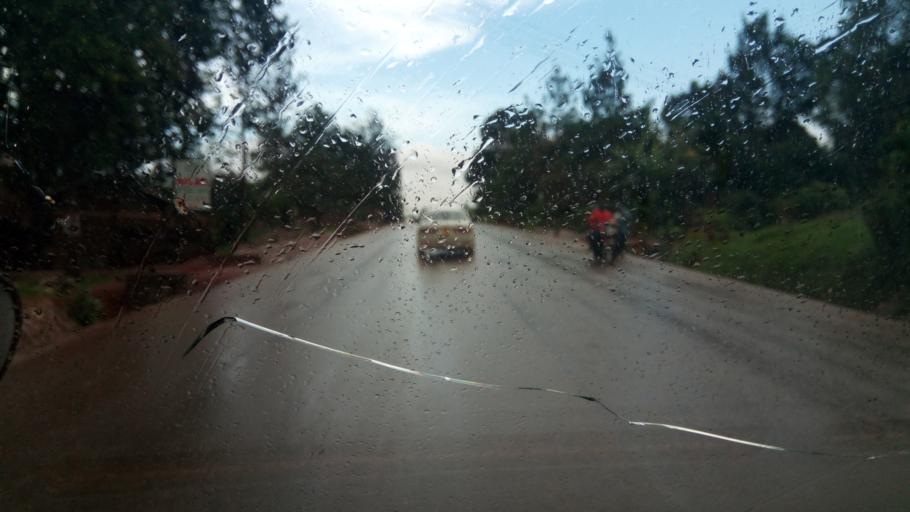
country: UG
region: Central Region
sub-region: Wakiso District
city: Wakiso
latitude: 0.3918
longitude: 32.5047
